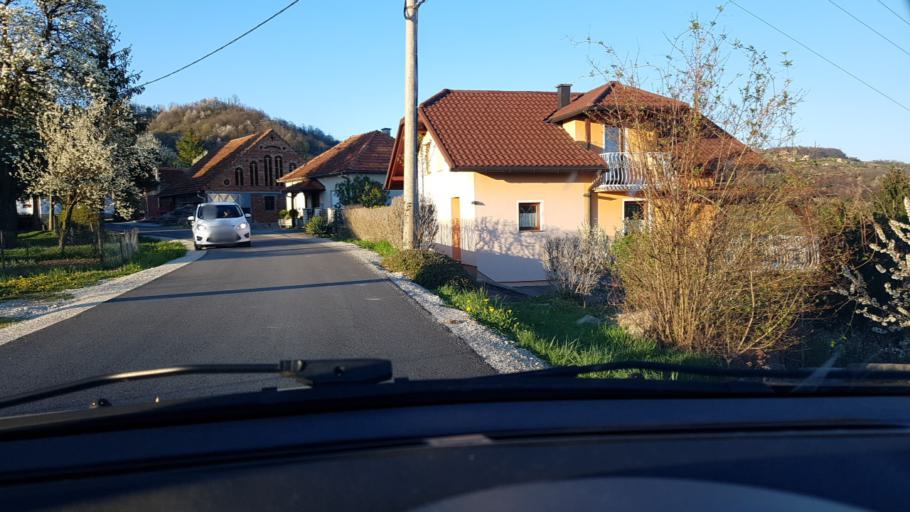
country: HR
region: Krapinsko-Zagorska
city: Pregrada
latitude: 46.1611
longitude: 15.7097
